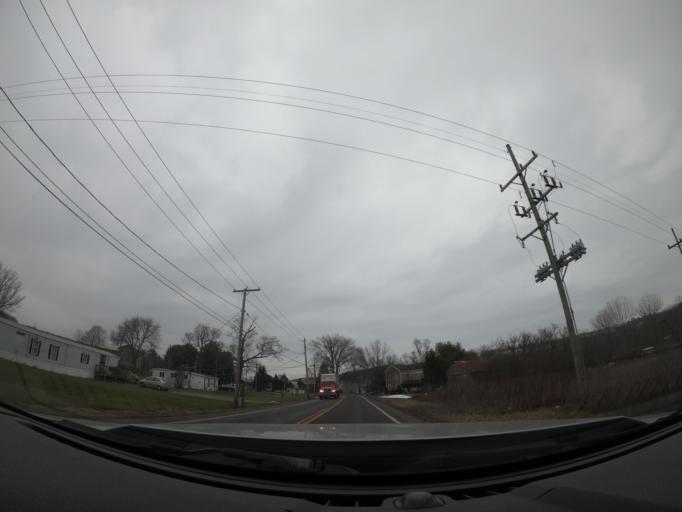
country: US
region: New York
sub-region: Cayuga County
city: Moravia
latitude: 42.6582
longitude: -76.4333
